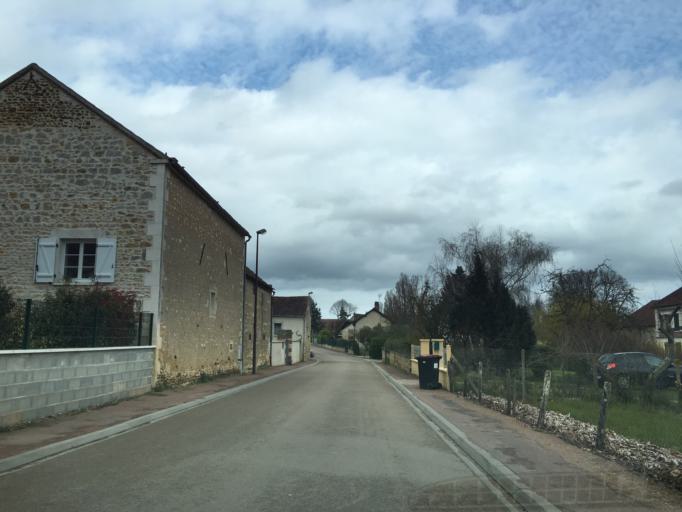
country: FR
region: Bourgogne
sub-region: Departement de l'Yonne
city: Charbuy
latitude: 47.8288
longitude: 3.4585
